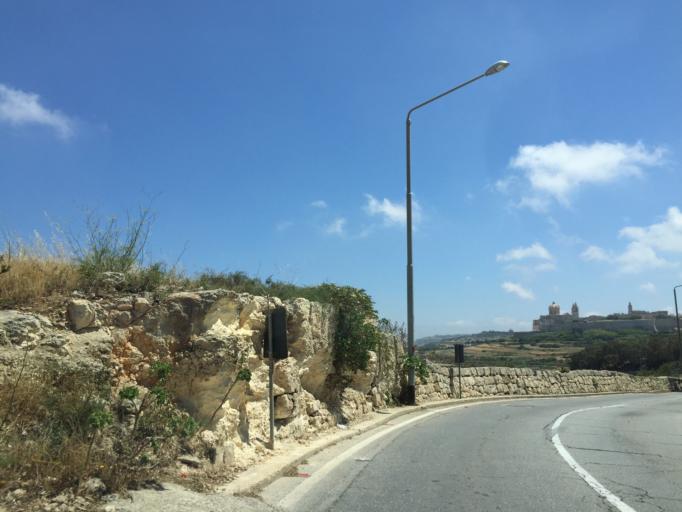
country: MT
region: L-Imtarfa
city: Imtarfa
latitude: 35.8957
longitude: 14.4036
